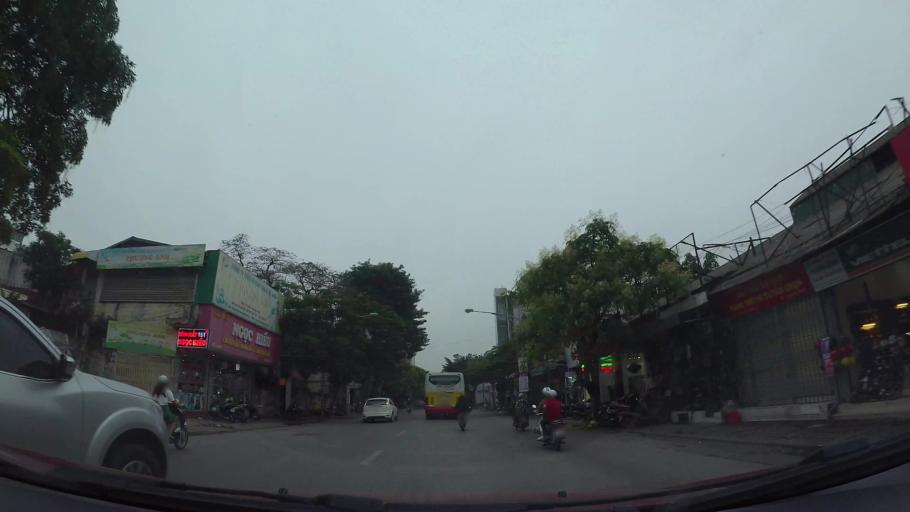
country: VN
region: Ha Noi
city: Hanoi
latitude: 21.0221
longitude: 105.8415
